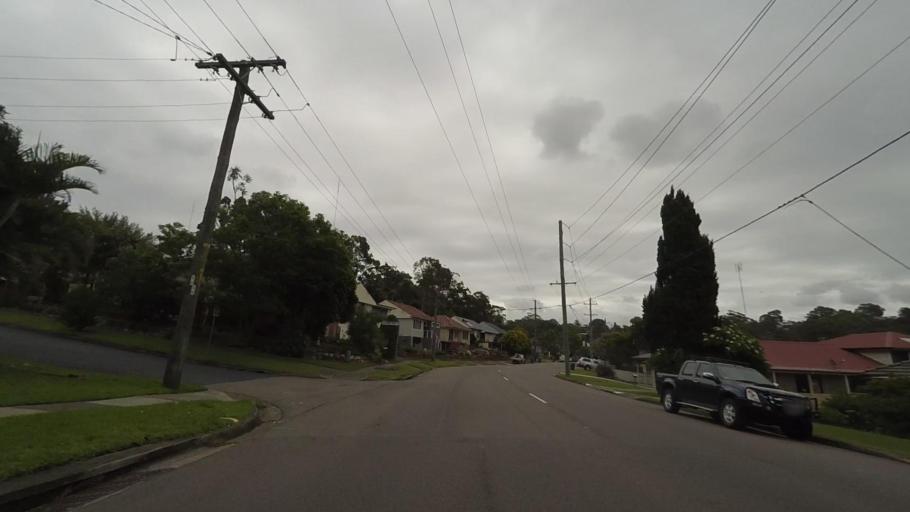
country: AU
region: New South Wales
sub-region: Lake Macquarie Shire
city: Kotara
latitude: -32.9451
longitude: 151.6930
